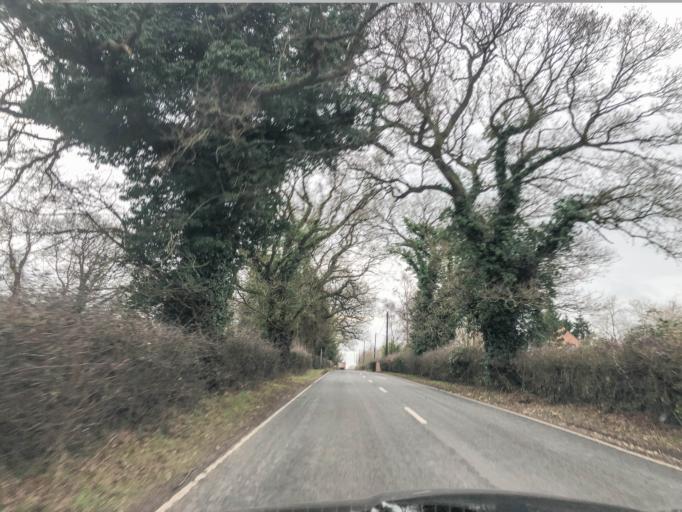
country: GB
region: England
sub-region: Warwickshire
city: Wroxall
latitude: 52.3167
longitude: -1.6736
